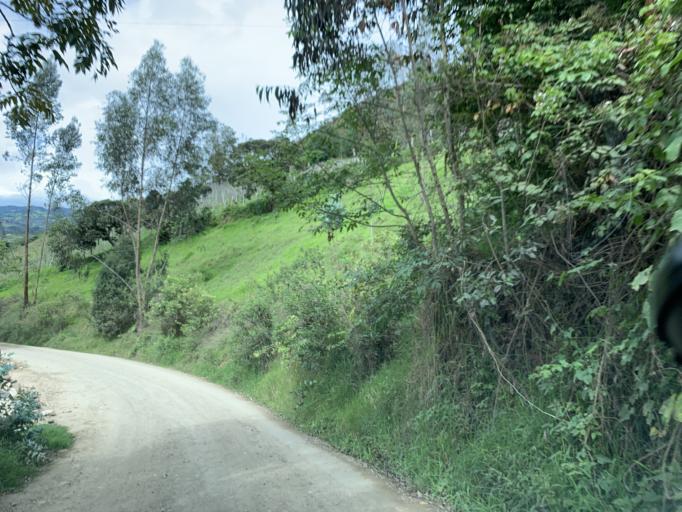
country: CO
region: Boyaca
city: Ramiriqui
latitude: 5.4117
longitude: -73.3306
